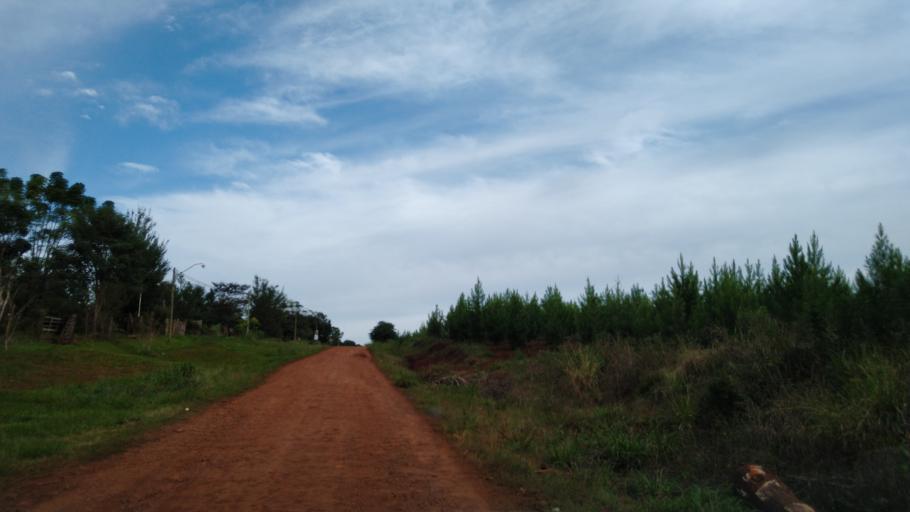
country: AR
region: Misiones
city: Capiovi
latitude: -26.9395
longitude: -55.0966
